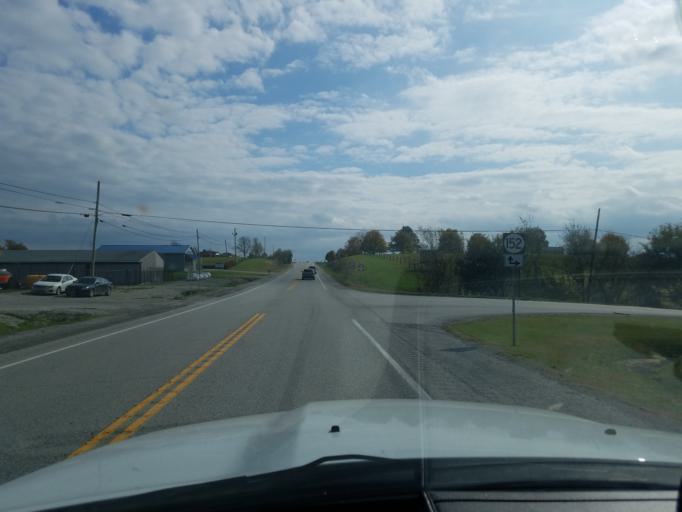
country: US
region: Kentucky
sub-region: Washington County
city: Springfield
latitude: 37.6984
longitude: -85.2485
